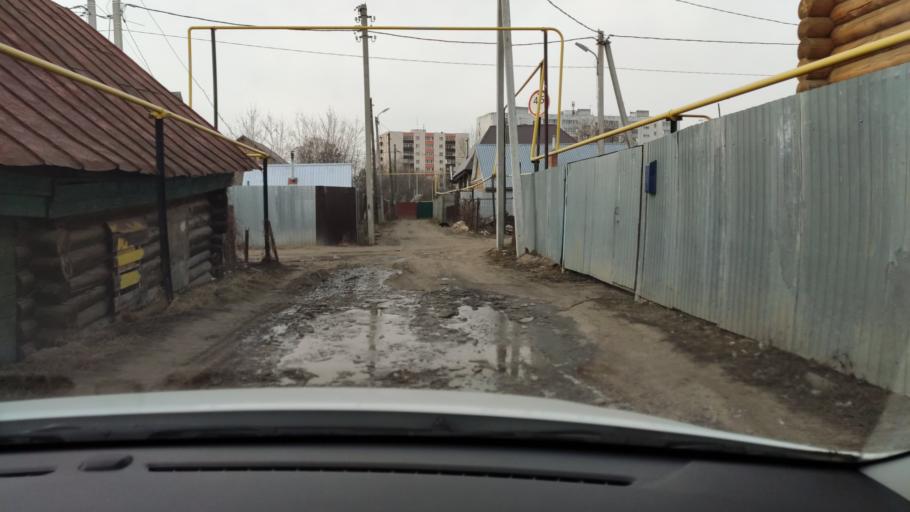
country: RU
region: Tatarstan
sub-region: Gorod Kazan'
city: Kazan
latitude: 55.7442
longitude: 49.1484
